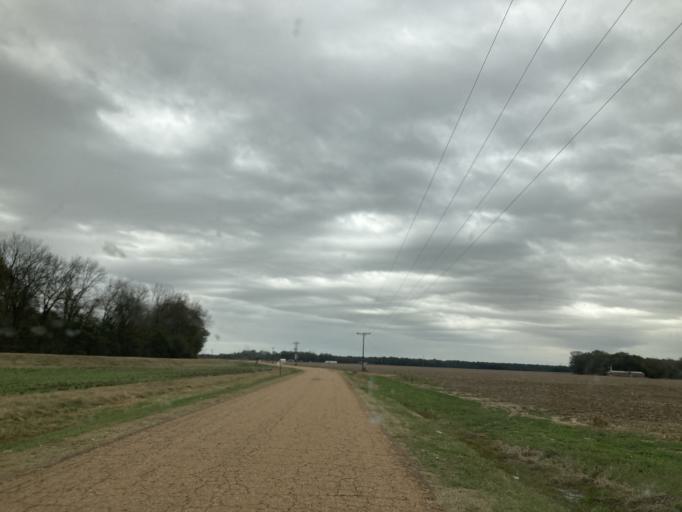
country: US
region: Mississippi
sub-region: Yazoo County
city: Yazoo City
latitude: 32.9800
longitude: -90.4206
